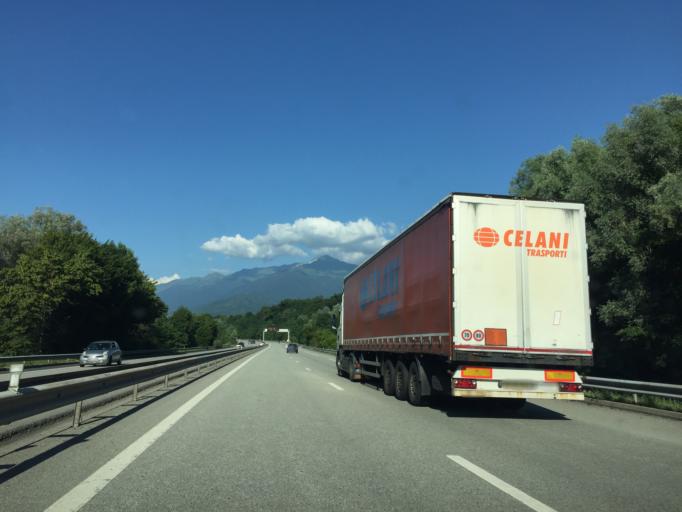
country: FR
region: Rhone-Alpes
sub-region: Departement de la Savoie
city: Coise-Saint-Jean-Pied-Gauthier
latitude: 45.5573
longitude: 6.1873
